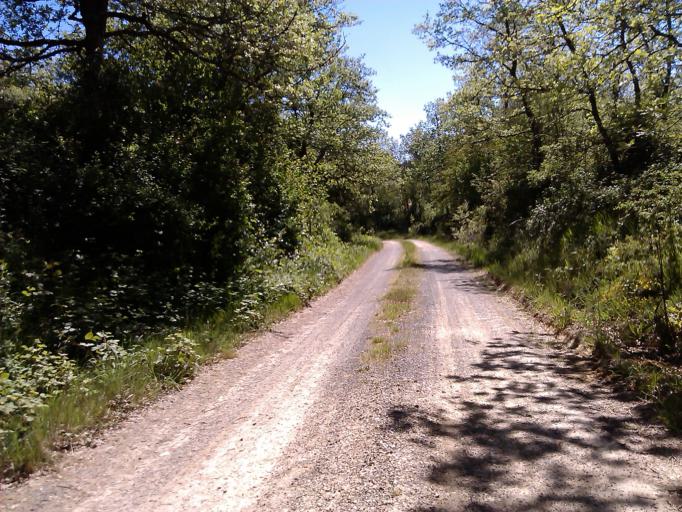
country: ES
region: Castille and Leon
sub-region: Provincia de Burgos
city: Barrios de Colina
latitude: 42.3734
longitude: -3.4393
